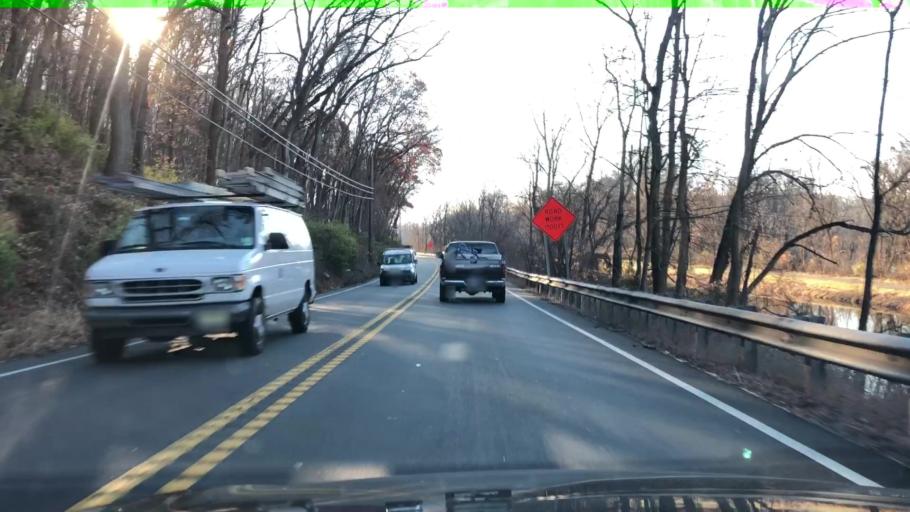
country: US
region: New Jersey
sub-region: Hunterdon County
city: Lambertville
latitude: 40.3459
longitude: -74.9427
